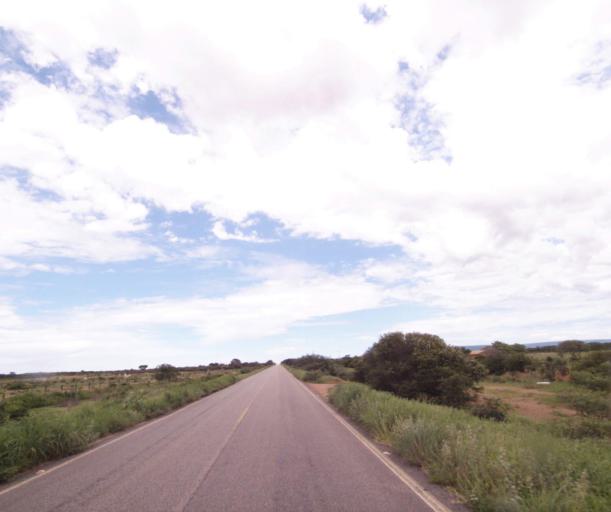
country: BR
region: Bahia
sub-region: Palmas De Monte Alto
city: Palmas de Monte Alto
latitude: -14.2566
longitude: -43.2504
